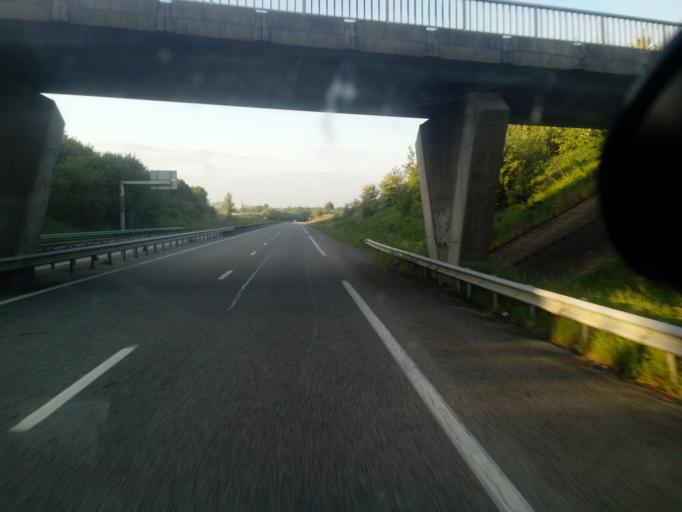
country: FR
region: Haute-Normandie
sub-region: Departement de la Seine-Maritime
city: Foucarmont
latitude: 49.8308
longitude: 1.5257
